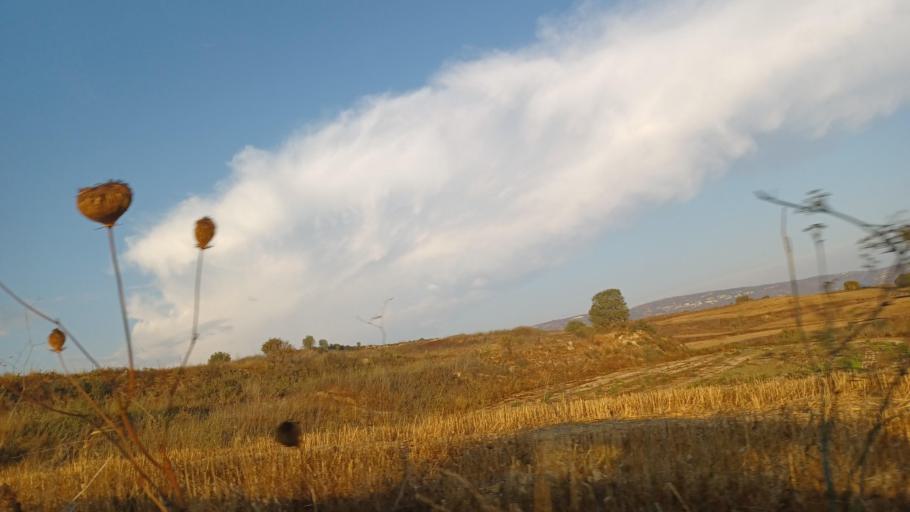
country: CY
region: Pafos
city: Tala
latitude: 34.9021
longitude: 32.4995
